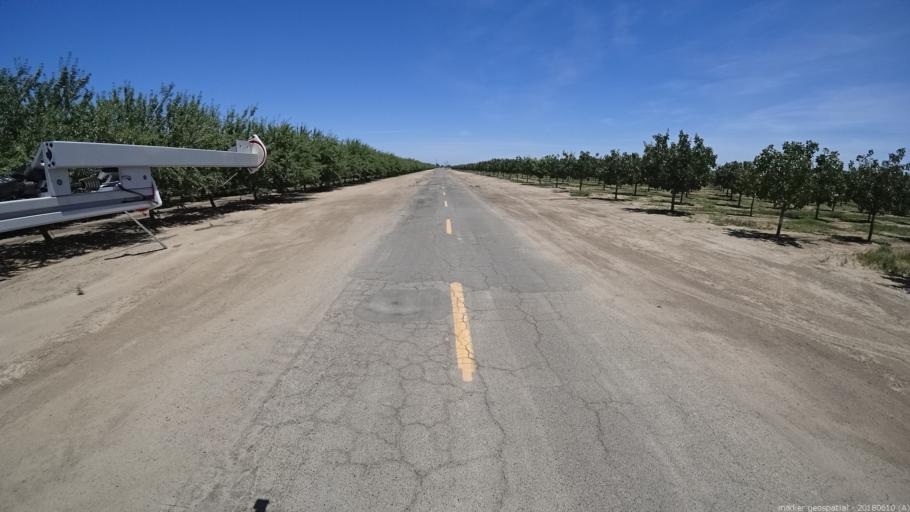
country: US
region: California
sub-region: Madera County
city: Chowchilla
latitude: 37.0688
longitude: -120.3535
